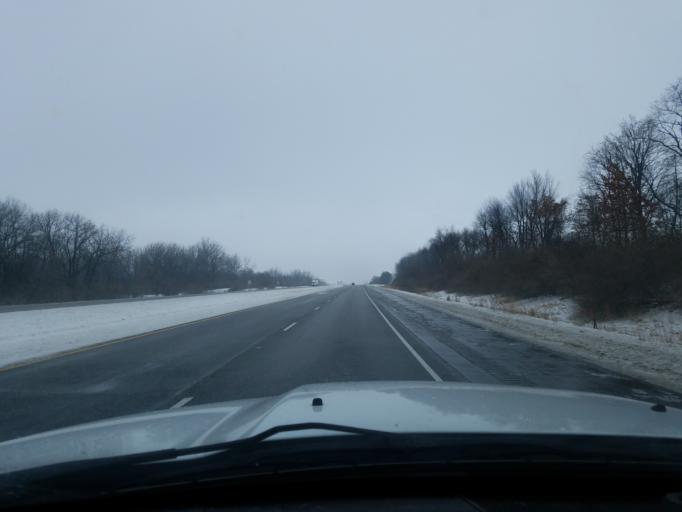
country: US
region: Indiana
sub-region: Fulton County
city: Rochester
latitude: 40.9350
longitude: -86.1682
